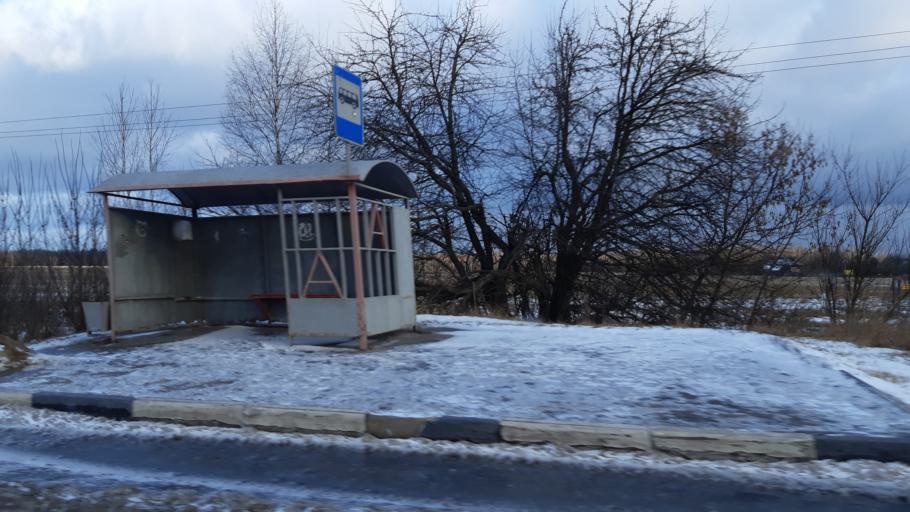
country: RU
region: Moskovskaya
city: Noginsk-9
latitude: 56.0234
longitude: 38.5563
